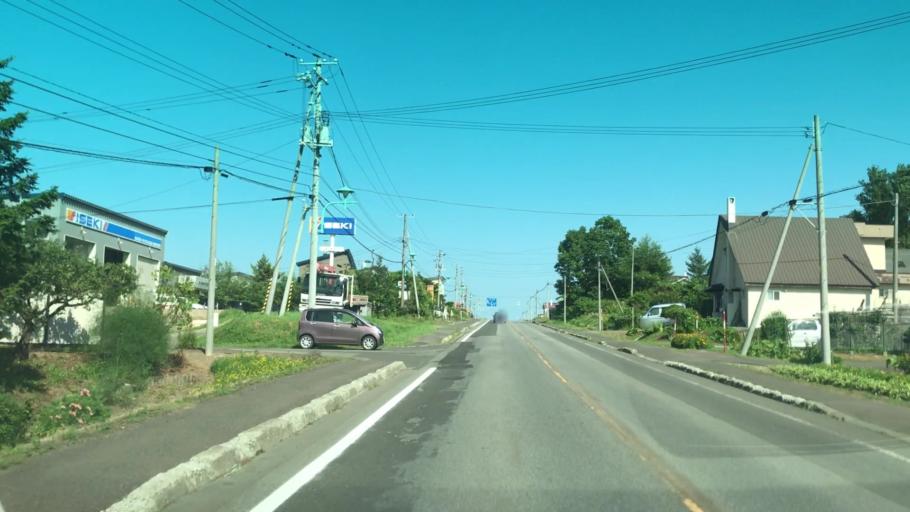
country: JP
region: Hokkaido
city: Iwanai
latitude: 42.9823
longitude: 140.5693
